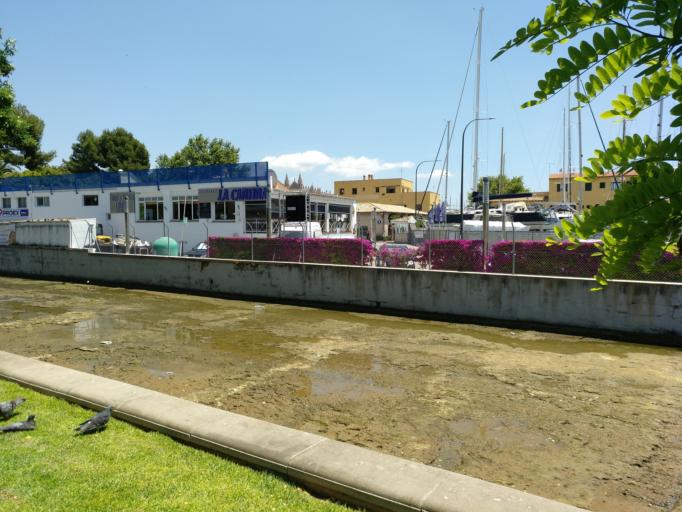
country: ES
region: Balearic Islands
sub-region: Illes Balears
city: Palma
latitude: 39.5688
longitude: 2.6389
